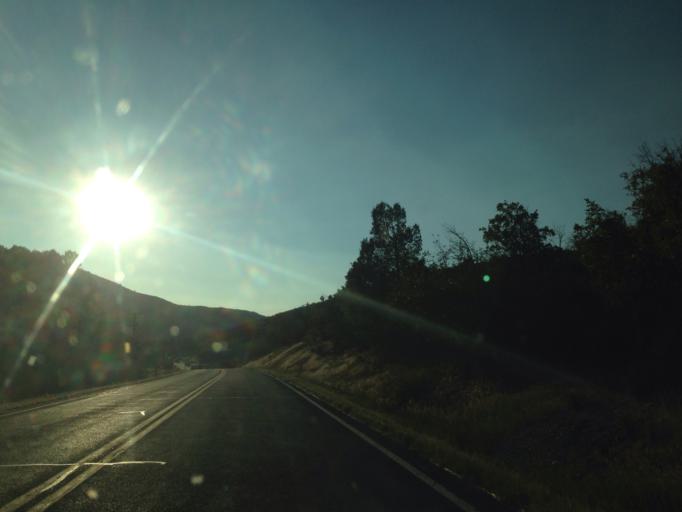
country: US
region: Utah
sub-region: Summit County
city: Francis
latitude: 40.6252
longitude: -111.2294
